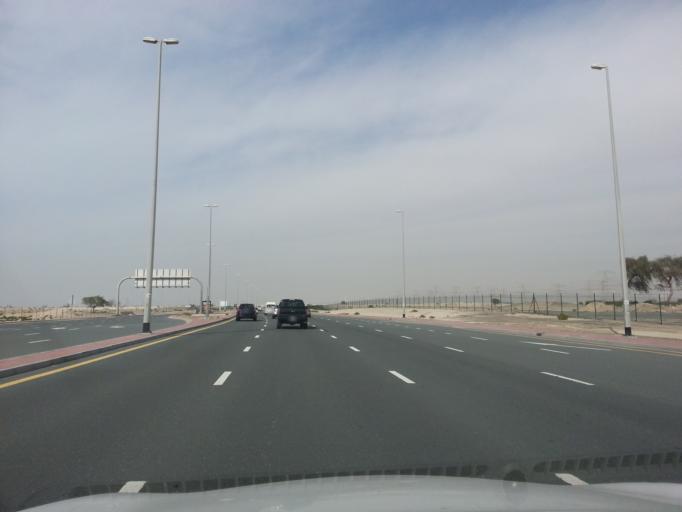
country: AE
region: Dubai
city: Dubai
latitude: 25.0689
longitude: 55.1937
